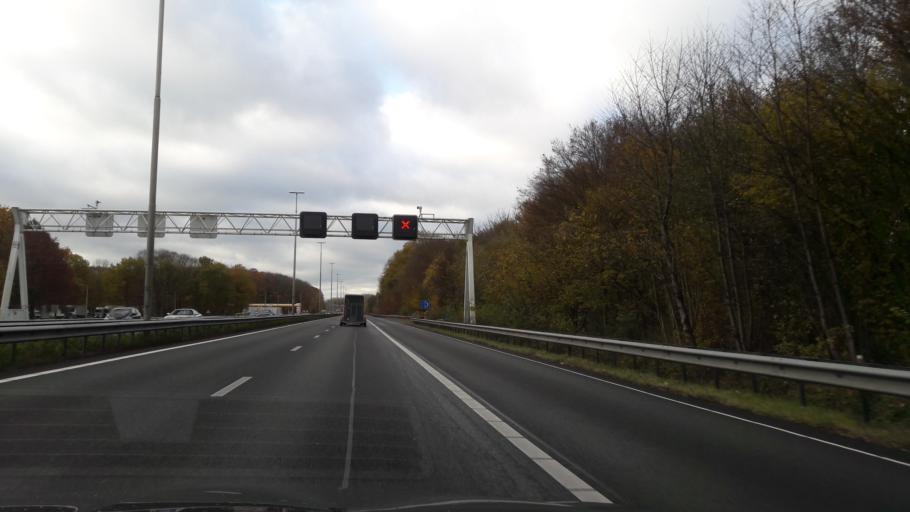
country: NL
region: Limburg
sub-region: Gemeente Sittard-Geleen
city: Born
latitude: 51.0137
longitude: 5.8024
